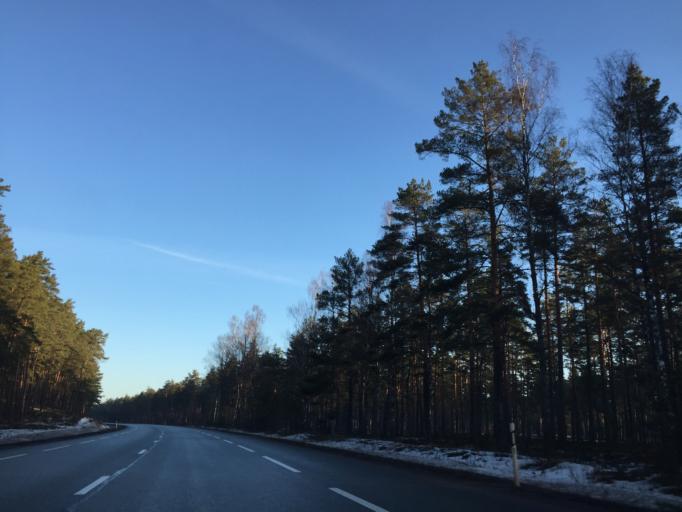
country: LV
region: Carnikava
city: Carnikava
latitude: 57.1572
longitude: 24.3462
